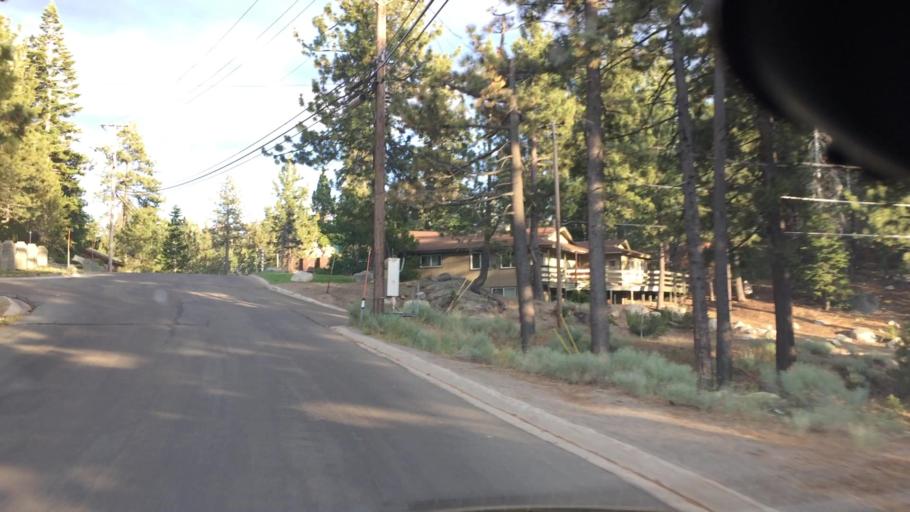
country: US
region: Nevada
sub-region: Douglas County
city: Kingsbury
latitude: 38.9716
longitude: -119.8901
